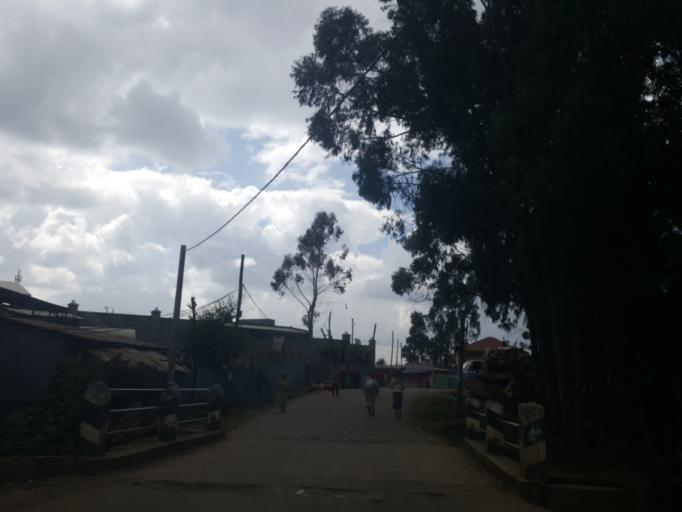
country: ET
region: Adis Abeba
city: Addis Ababa
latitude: 9.0651
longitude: 38.7178
